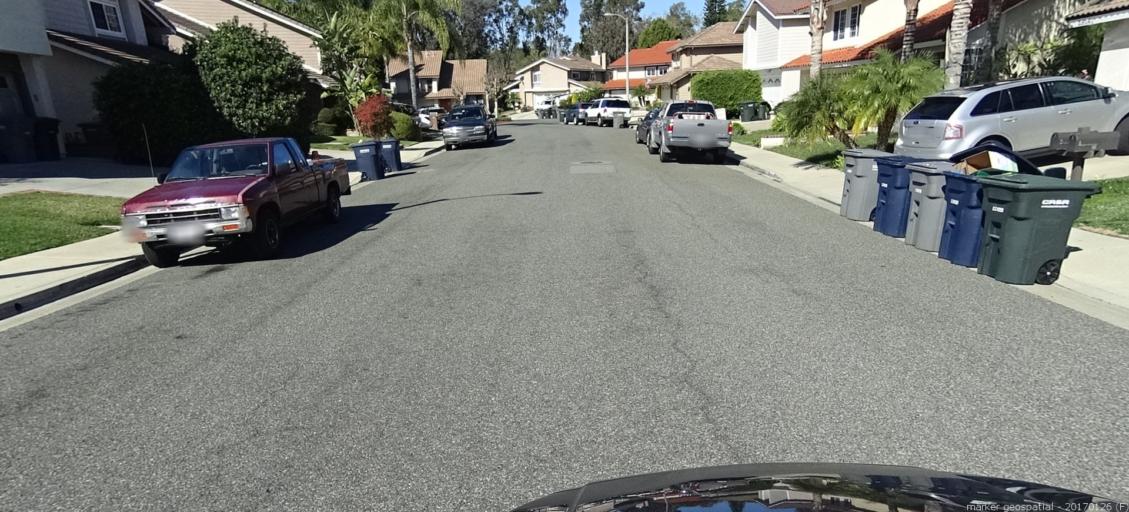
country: US
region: California
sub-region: Orange County
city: Lake Forest
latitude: 33.6356
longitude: -117.6746
